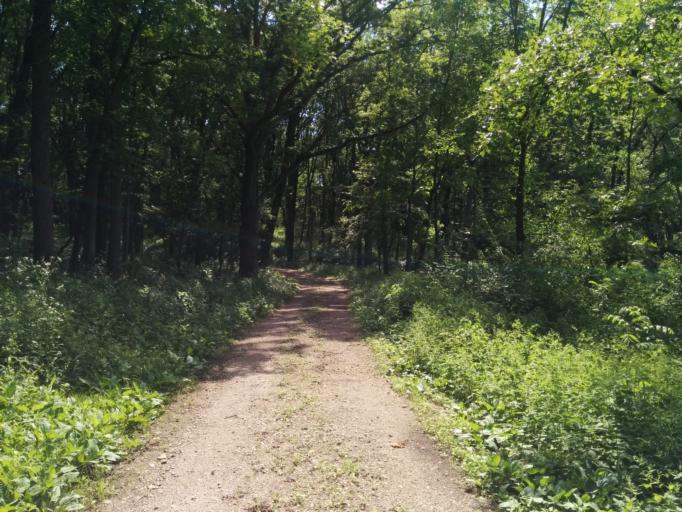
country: US
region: Illinois
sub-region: Will County
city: Goodings Grove
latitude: 41.6841
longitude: -87.8992
